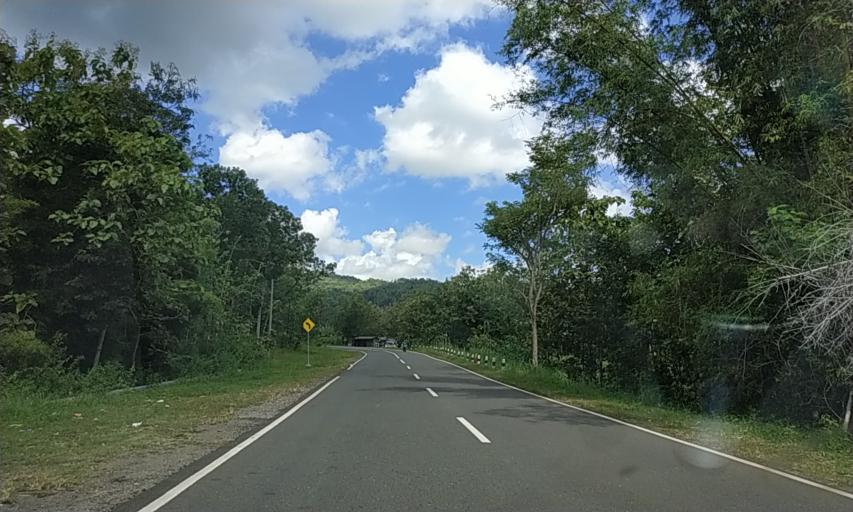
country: ID
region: East Java
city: Krajan
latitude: -8.0387
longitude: 110.9435
